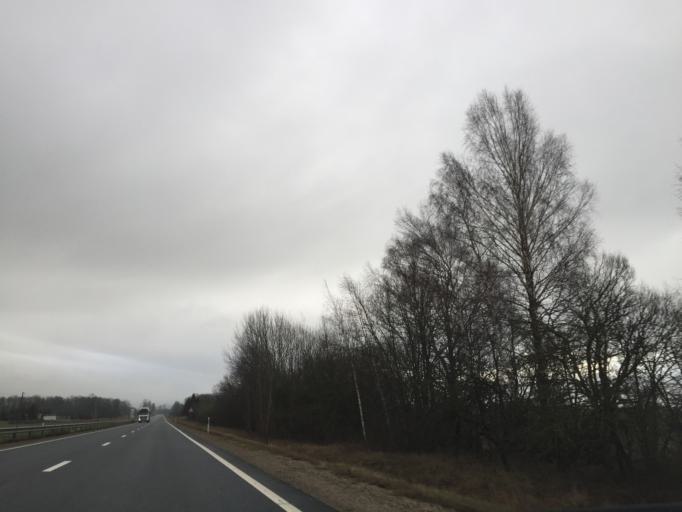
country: LV
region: Durbe
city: Liegi
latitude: 56.5901
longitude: 21.4129
